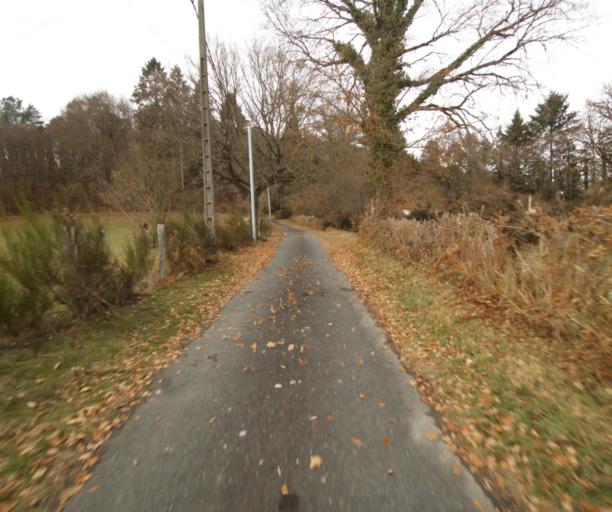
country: FR
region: Limousin
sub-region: Departement de la Correze
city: Chameyrat
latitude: 45.2428
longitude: 1.6828
